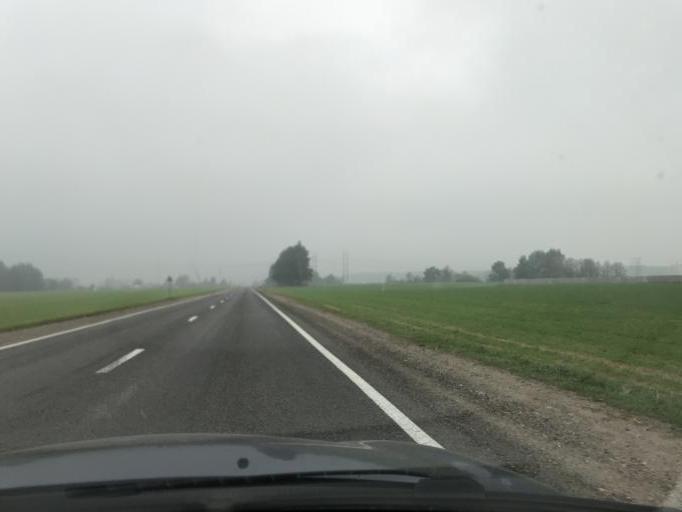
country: BY
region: Grodnenskaya
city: Hrodna
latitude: 53.8273
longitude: 23.8790
